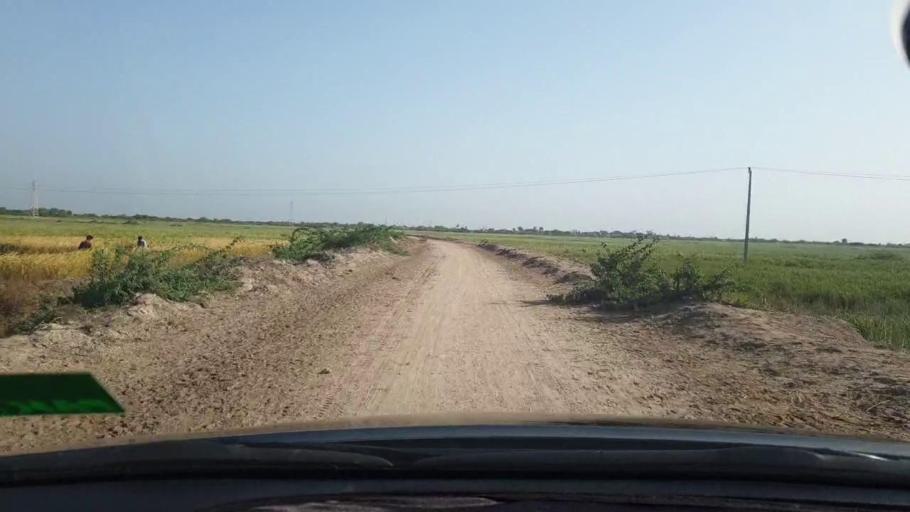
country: PK
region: Sindh
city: Tando Bago
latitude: 24.7130
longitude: 68.9512
